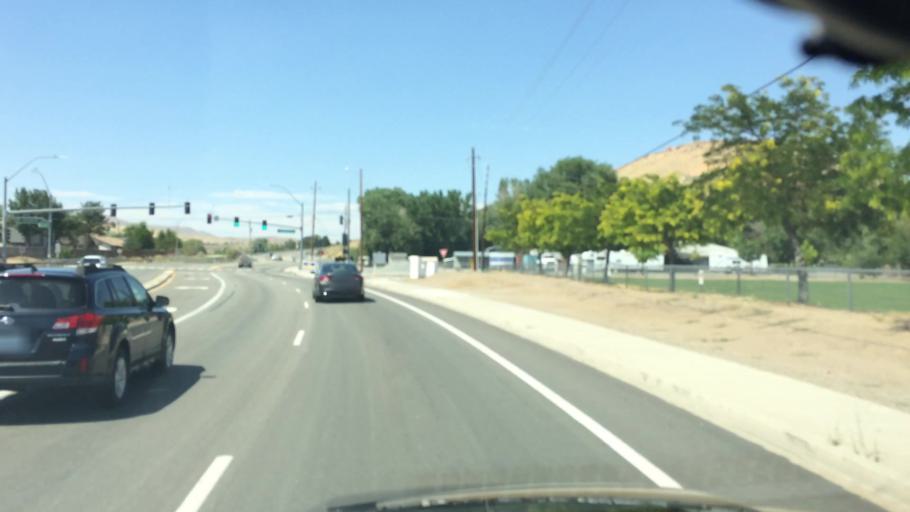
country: US
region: Nevada
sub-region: Washoe County
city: Sparks
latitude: 39.5626
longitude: -119.7244
